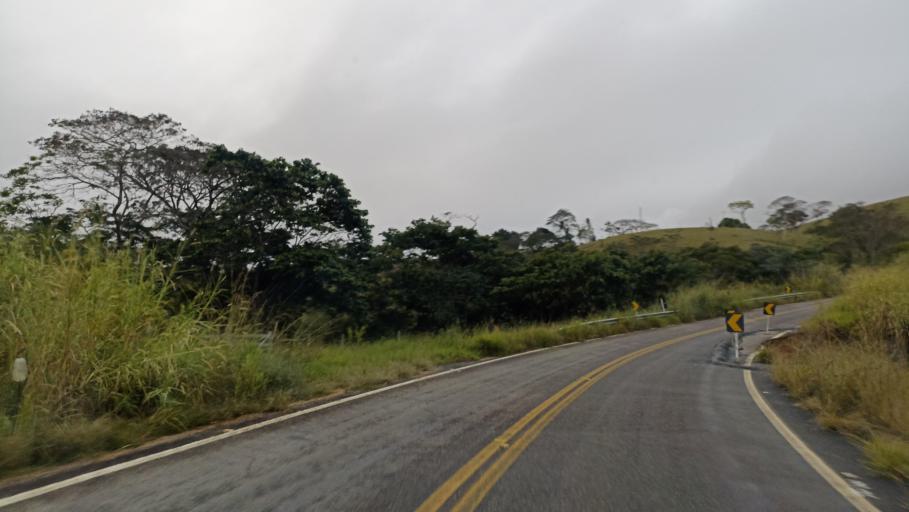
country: BR
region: Minas Gerais
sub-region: Joaima
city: Joaima
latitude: -16.6733
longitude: -40.5275
